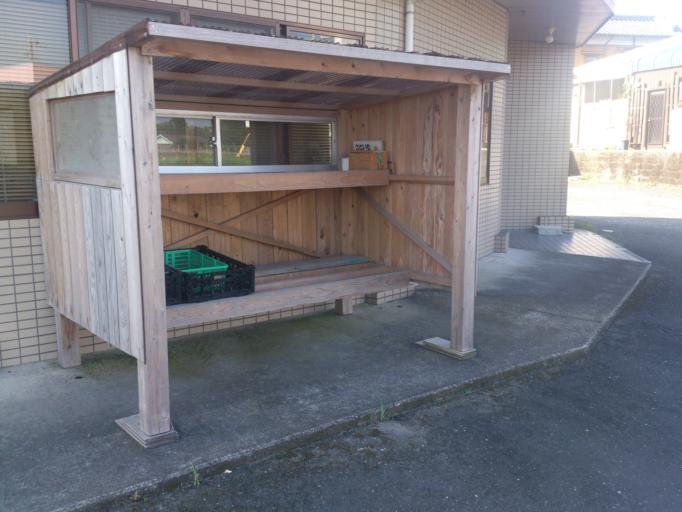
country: JP
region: Kagoshima
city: Kanoya
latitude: 31.3450
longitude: 130.9353
